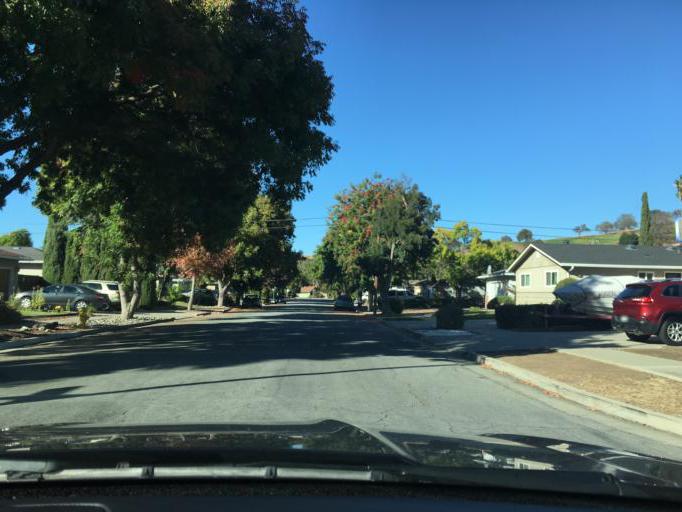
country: US
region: California
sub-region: Santa Clara County
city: Seven Trees
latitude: 37.2275
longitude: -121.8669
